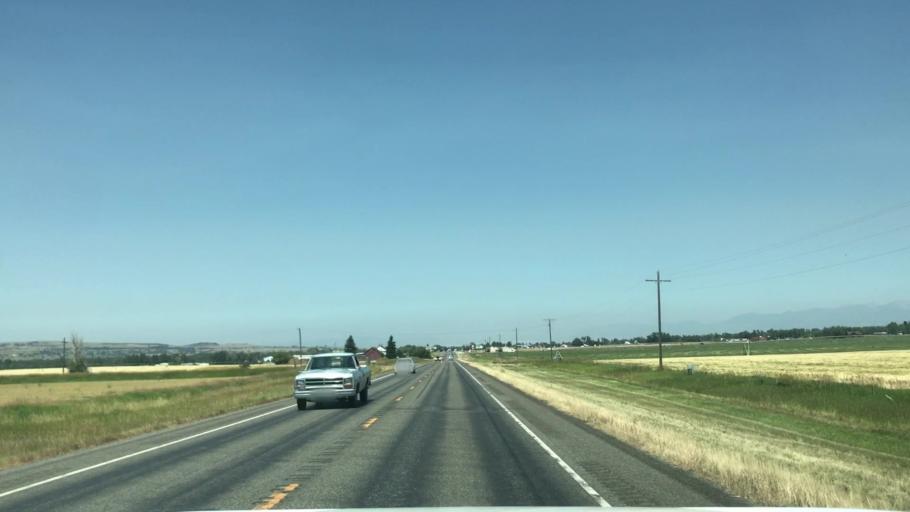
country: US
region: Montana
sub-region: Gallatin County
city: Four Corners
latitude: 45.5748
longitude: -111.1969
